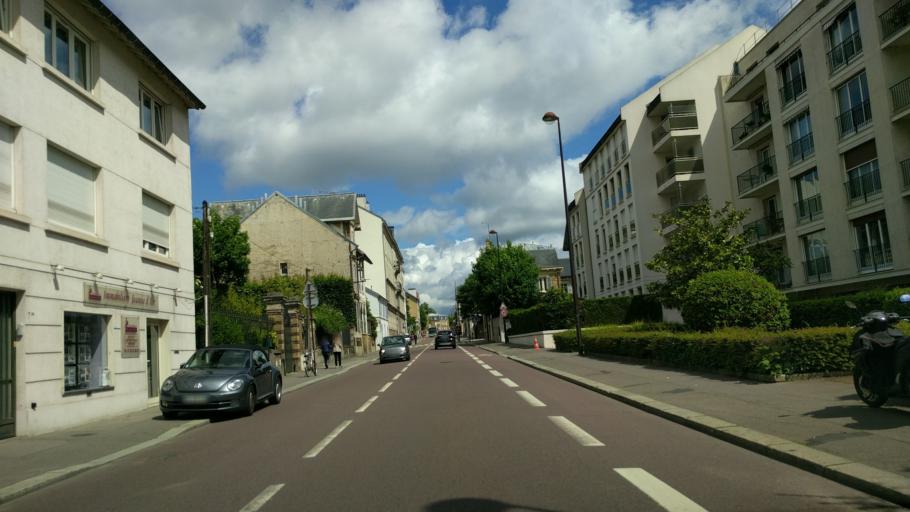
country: FR
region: Ile-de-France
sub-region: Departement des Yvelines
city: Versailles
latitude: 48.8151
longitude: 2.1363
